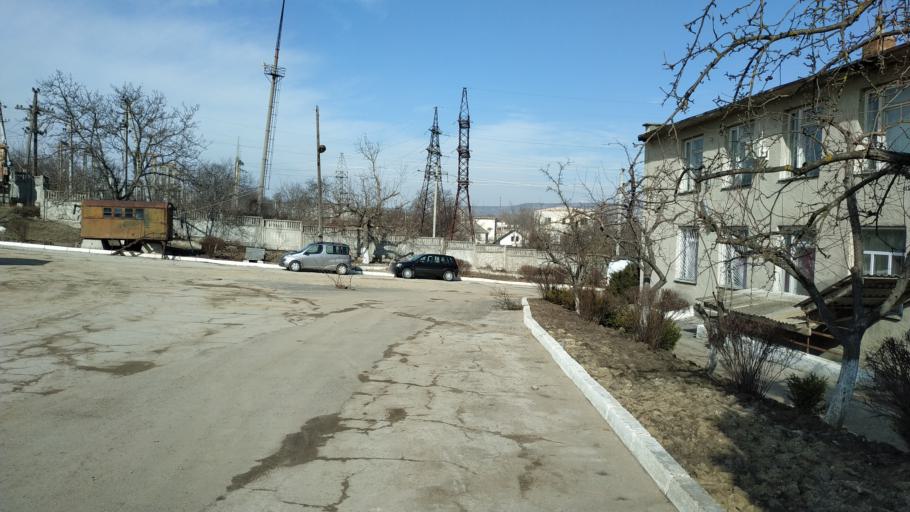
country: MD
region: Nisporeni
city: Nisporeni
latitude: 47.0601
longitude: 28.1695
